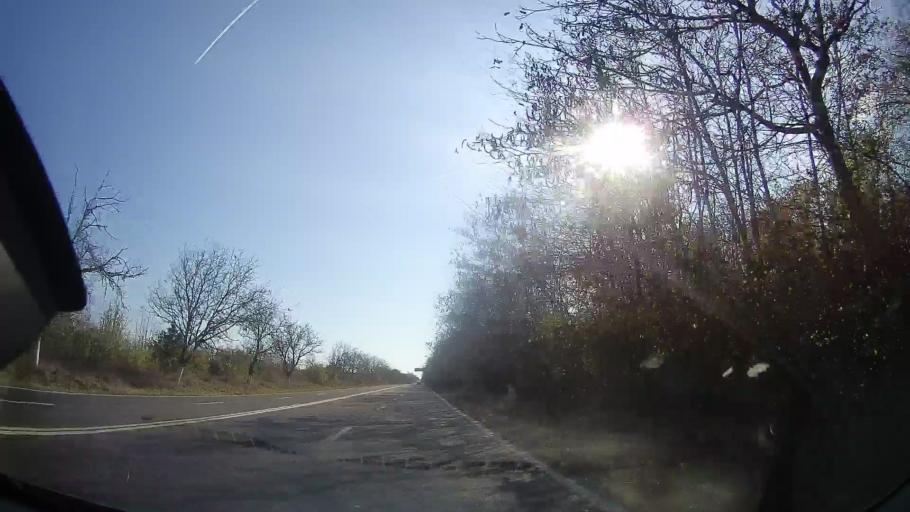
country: RO
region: Constanta
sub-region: Comuna Douazeci si Trei August
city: Dulcesti
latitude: 43.8831
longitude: 28.5732
